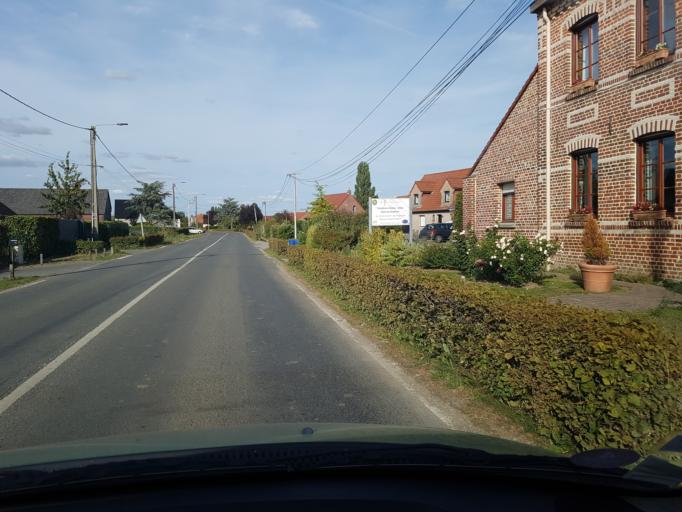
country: FR
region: Nord-Pas-de-Calais
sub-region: Departement du Pas-de-Calais
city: Locon
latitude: 50.5843
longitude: 2.6789
